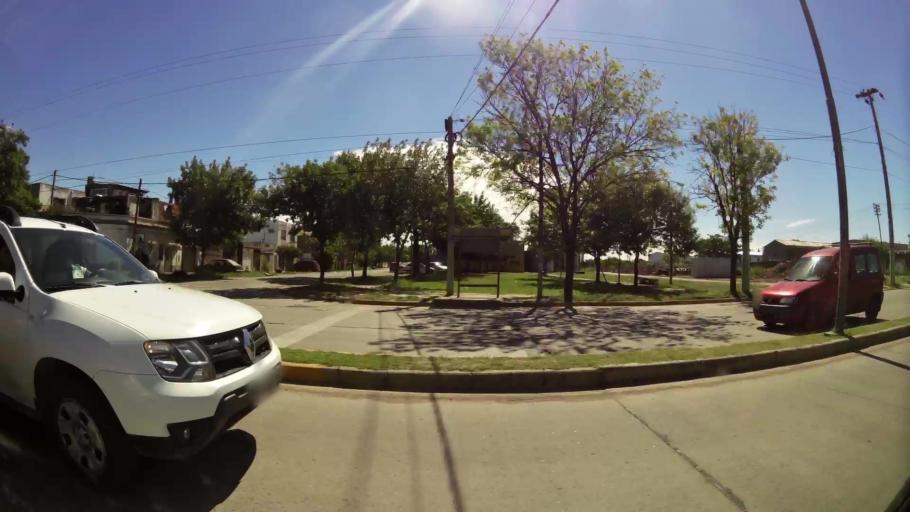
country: AR
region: Santa Fe
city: Granadero Baigorria
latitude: -32.9293
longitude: -60.7132
